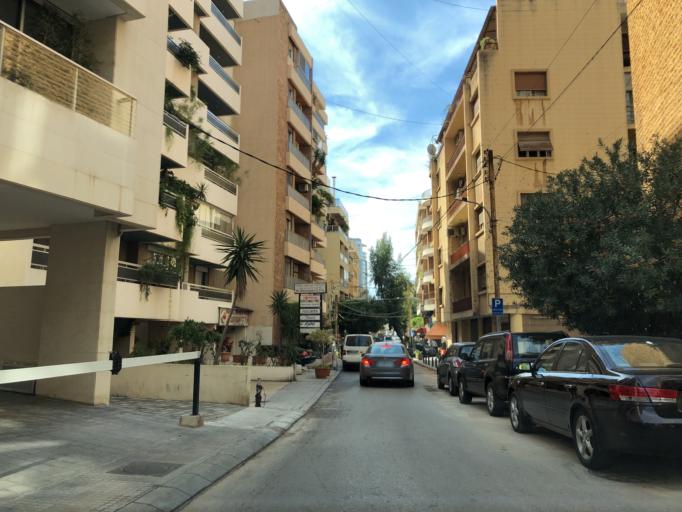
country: LB
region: Beyrouth
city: Beirut
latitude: 33.8858
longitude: 35.5173
